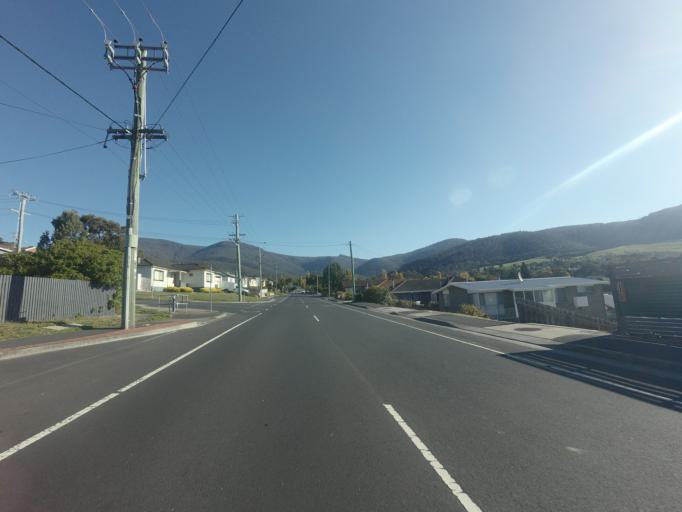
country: AU
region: Tasmania
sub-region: Glenorchy
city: Glenorchy
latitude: -42.8472
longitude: 147.2626
